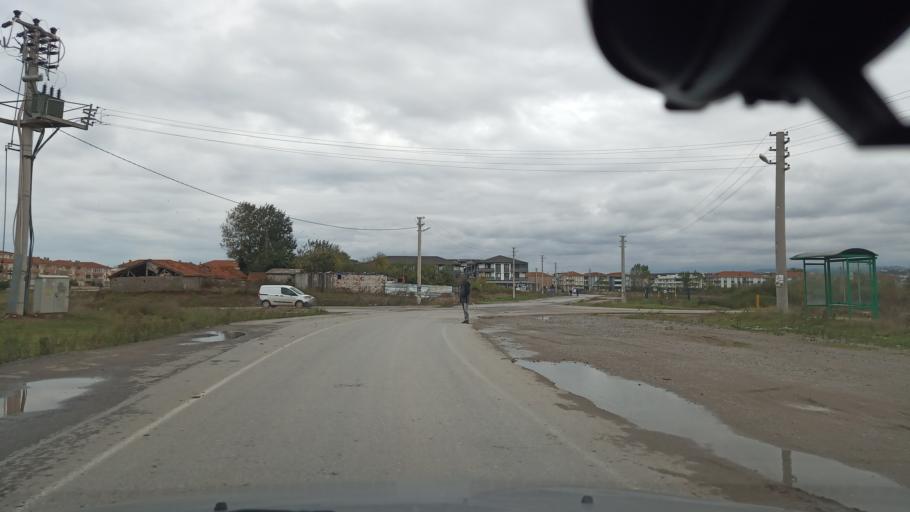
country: TR
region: Sakarya
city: Karasu
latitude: 41.1135
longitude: 30.6751
